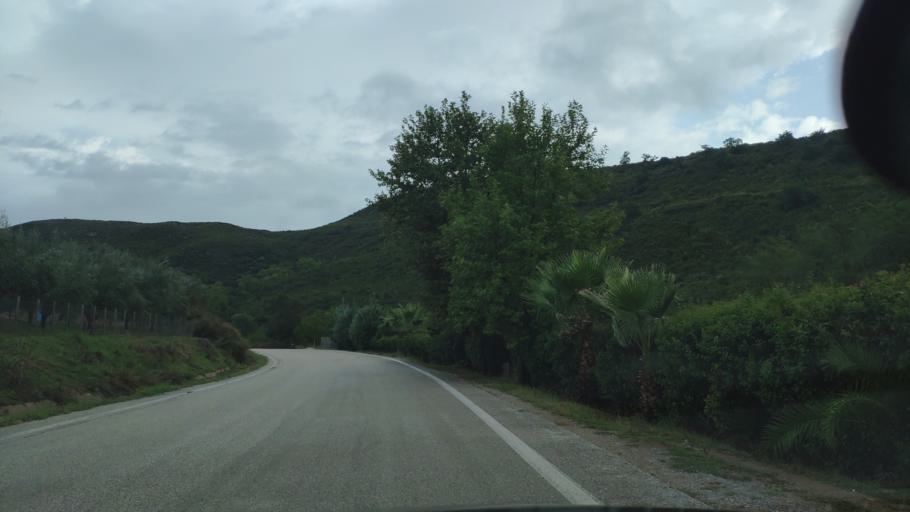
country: GR
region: West Greece
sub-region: Nomos Aitolias kai Akarnanias
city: Sardinia
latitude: 38.9125
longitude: 21.3557
